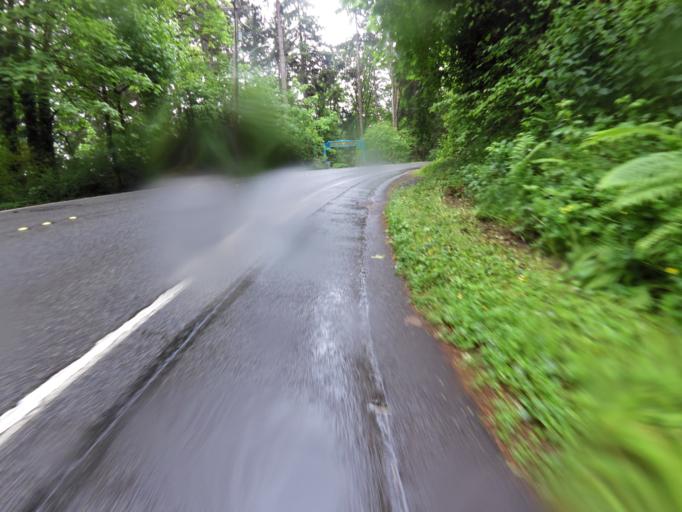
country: US
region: Washington
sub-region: King County
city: Mercer Island
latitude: 47.5436
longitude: -122.2129
